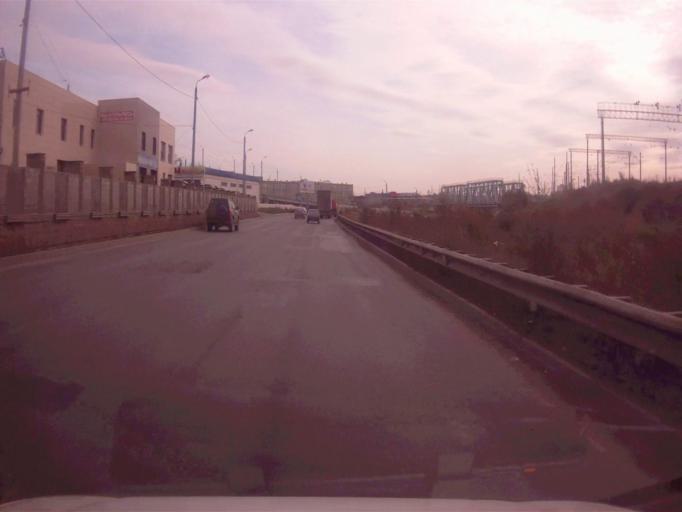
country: RU
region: Chelyabinsk
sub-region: Gorod Chelyabinsk
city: Chelyabinsk
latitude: 55.1573
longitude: 61.4406
